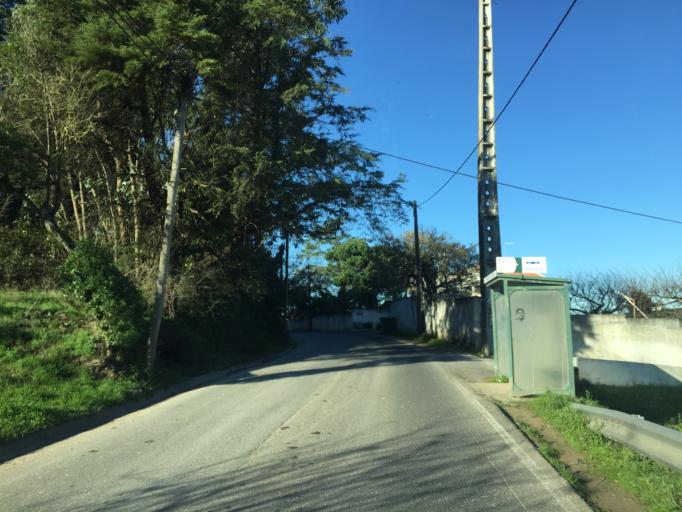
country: PT
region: Lisbon
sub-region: Odivelas
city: Canecas
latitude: 38.8245
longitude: -9.2411
